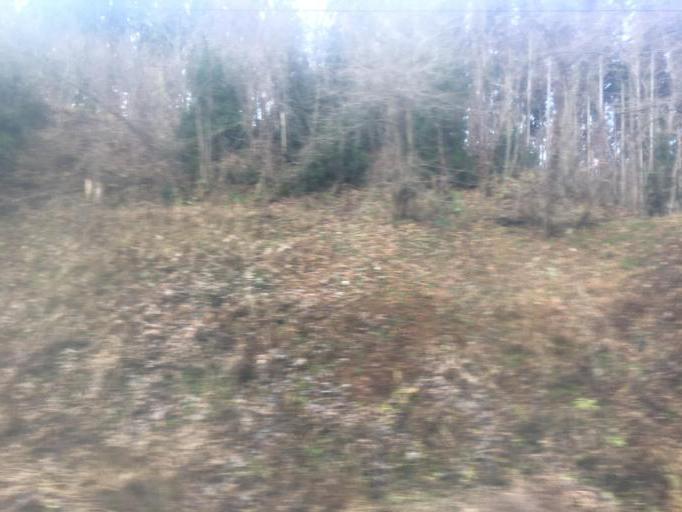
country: JP
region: Akita
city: Takanosu
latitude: 40.2598
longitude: 140.4052
